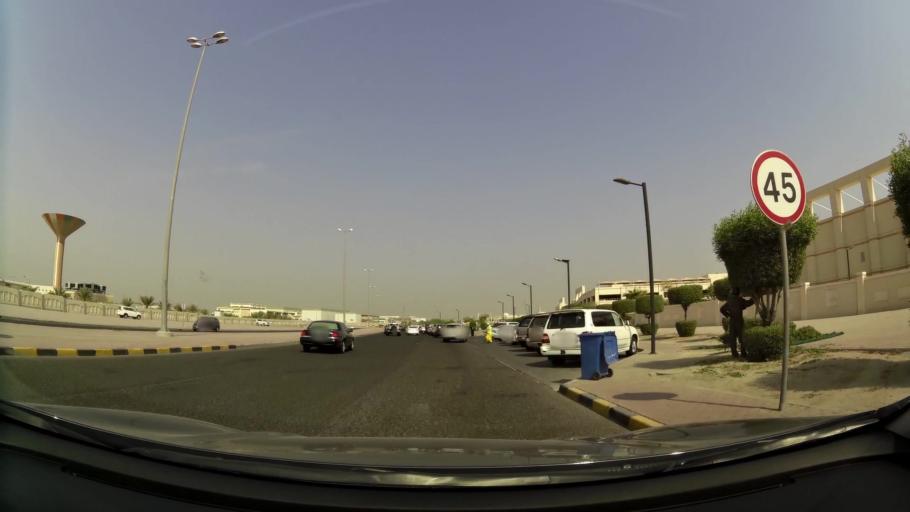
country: KW
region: Al Asimah
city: Ar Rabiyah
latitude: 29.2757
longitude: 47.9157
